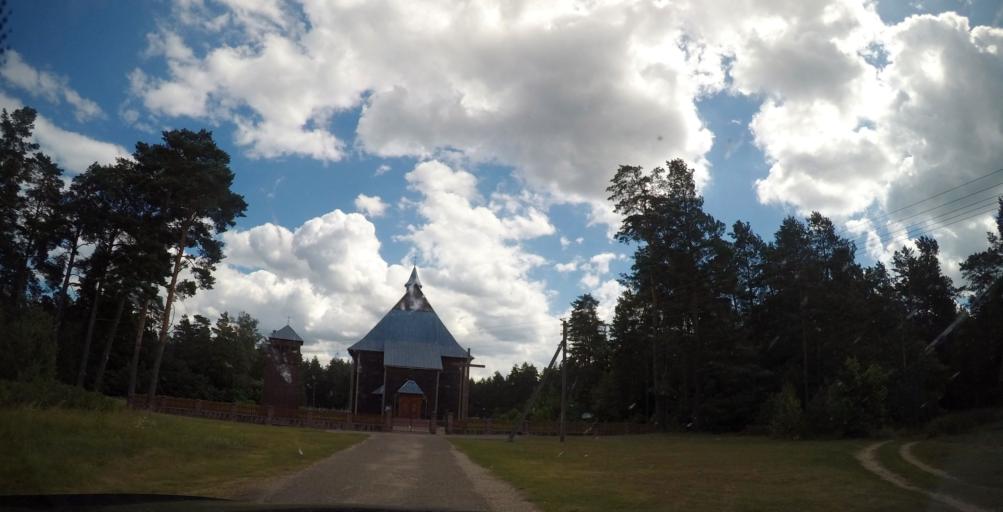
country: BY
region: Grodnenskaya
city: Skidal'
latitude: 53.8203
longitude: 24.2505
